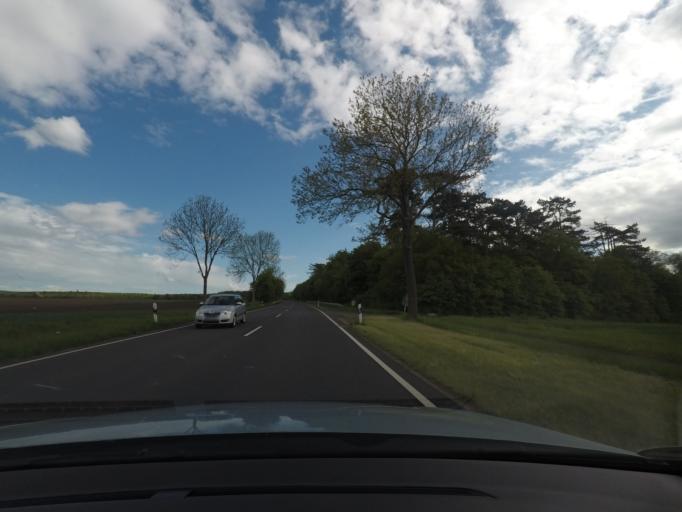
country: DE
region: Lower Saxony
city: Querenhorst
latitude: 52.3258
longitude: 10.9715
